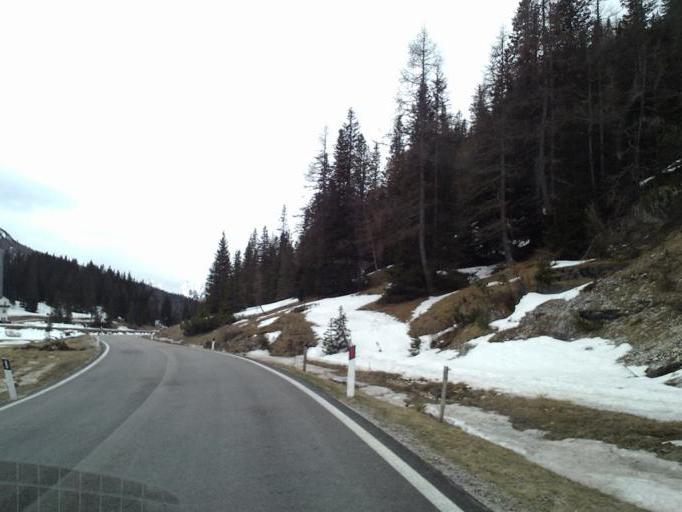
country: IT
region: Veneto
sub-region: Provincia di Belluno
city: Cortina d'Ampezzo
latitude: 46.5901
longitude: 12.2526
